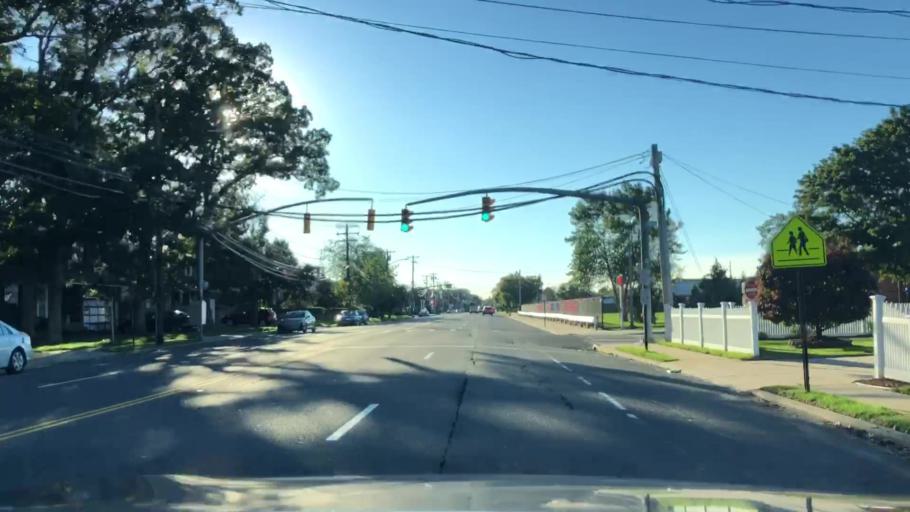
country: US
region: New York
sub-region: Nassau County
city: Massapequa
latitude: 40.6918
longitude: -73.4744
